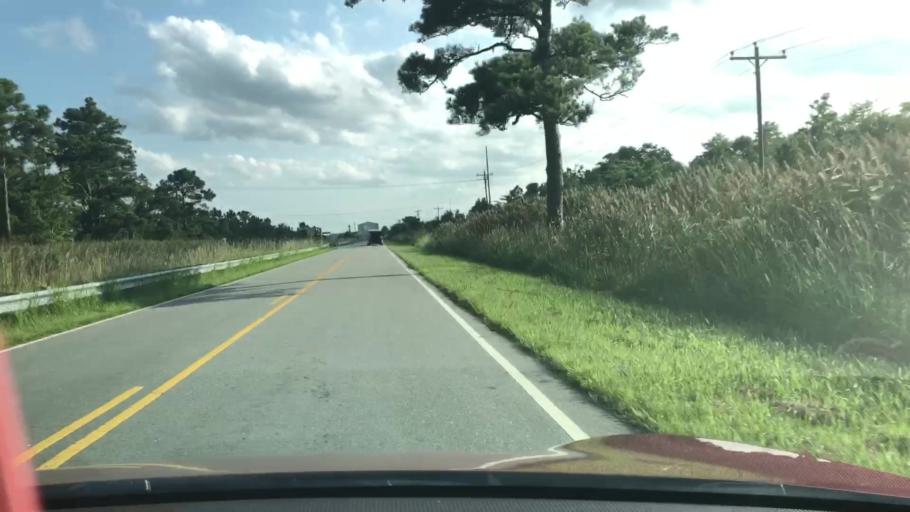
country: US
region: North Carolina
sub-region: Dare County
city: Wanchese
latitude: 35.7015
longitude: -75.7711
